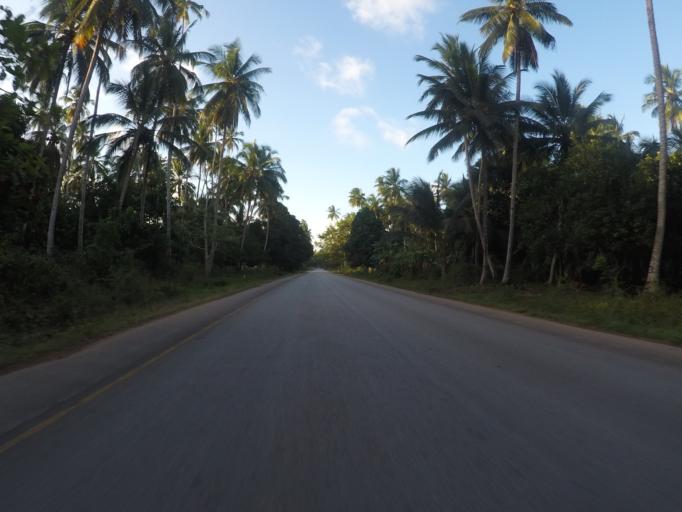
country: TZ
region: Zanzibar Central/South
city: Koani
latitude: -6.2001
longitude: 39.3257
